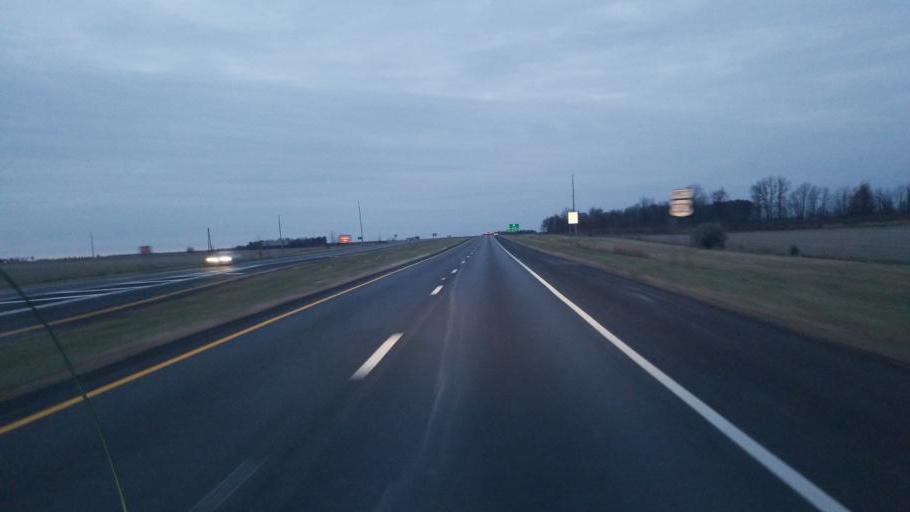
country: US
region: Ohio
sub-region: Hardin County
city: Forest
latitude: 40.8269
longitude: -83.4922
